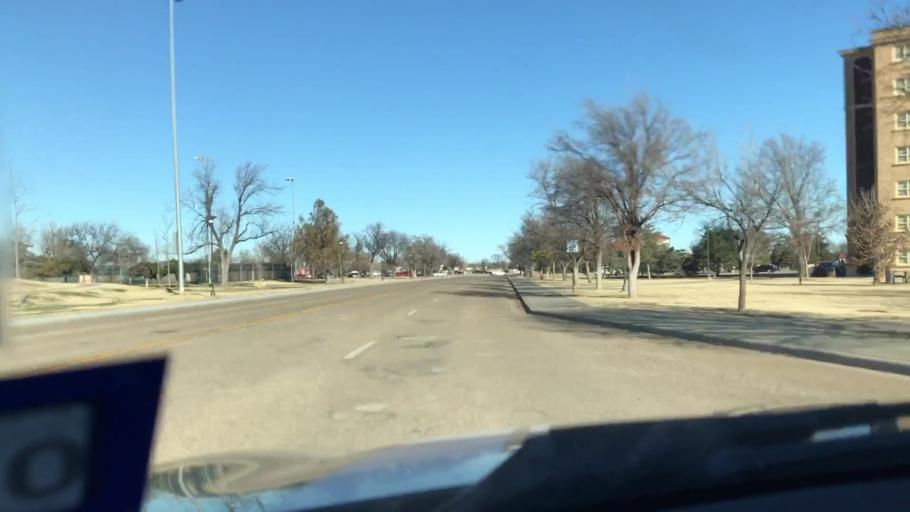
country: US
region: Texas
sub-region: Lubbock County
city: Lubbock
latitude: 33.5832
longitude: -101.8817
